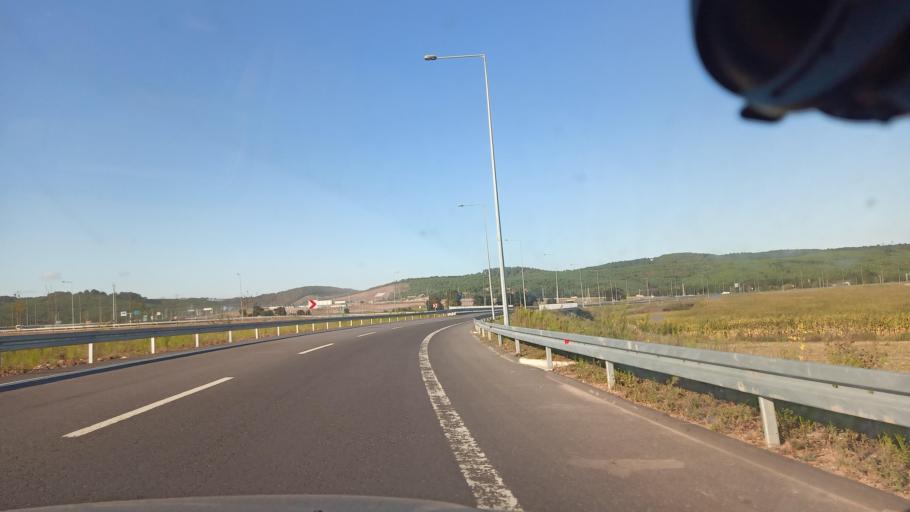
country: TR
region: Sakarya
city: Kazimpasa
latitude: 40.8373
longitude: 30.3531
